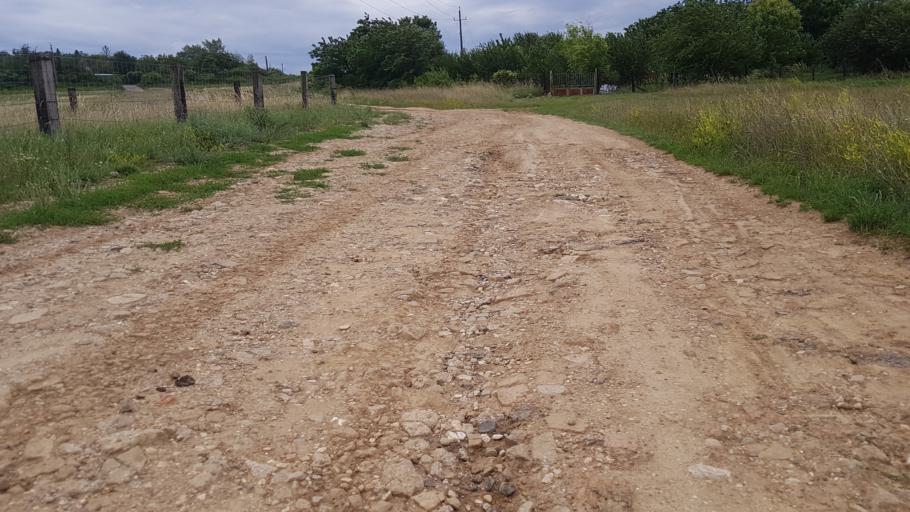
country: HU
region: Pest
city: Urom
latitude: 47.6104
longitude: 19.0274
